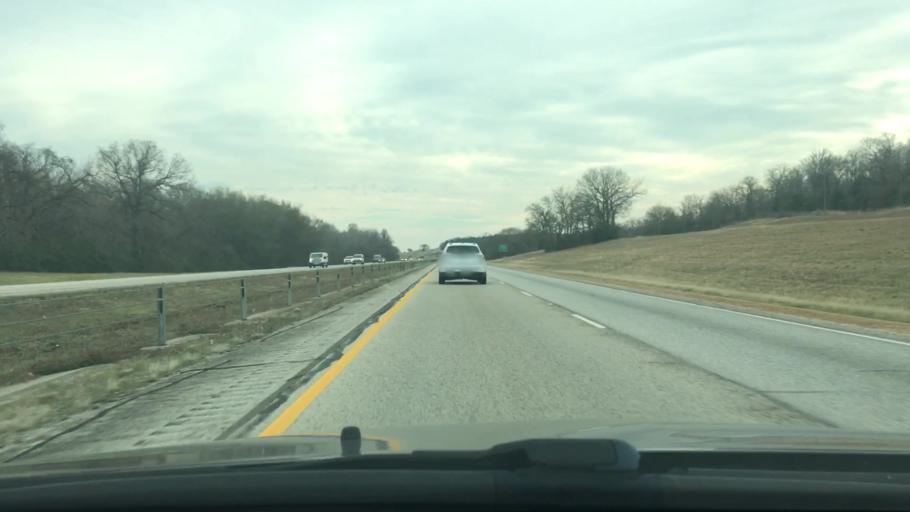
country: US
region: Texas
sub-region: Leon County
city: Centerville
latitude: 31.3015
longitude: -96.0002
